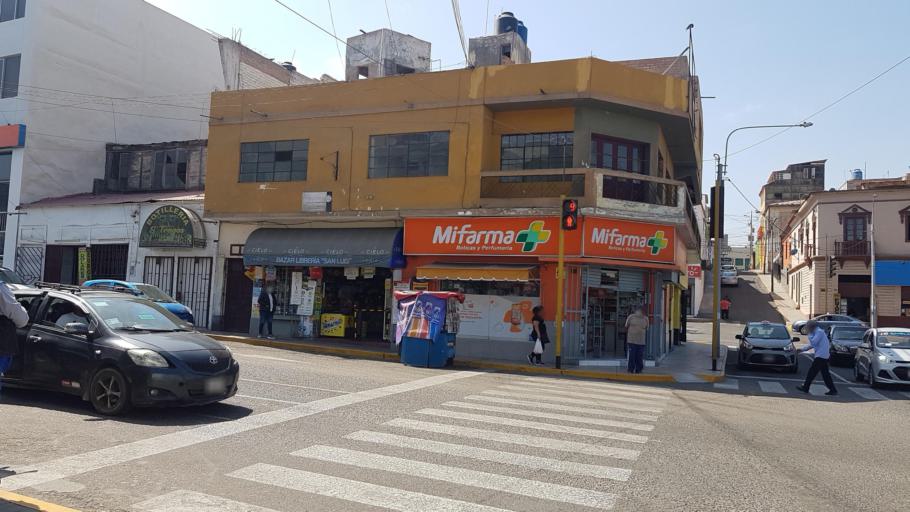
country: PE
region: Arequipa
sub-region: Provincia de Islay
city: Mollendo
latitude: -17.0292
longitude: -72.0158
